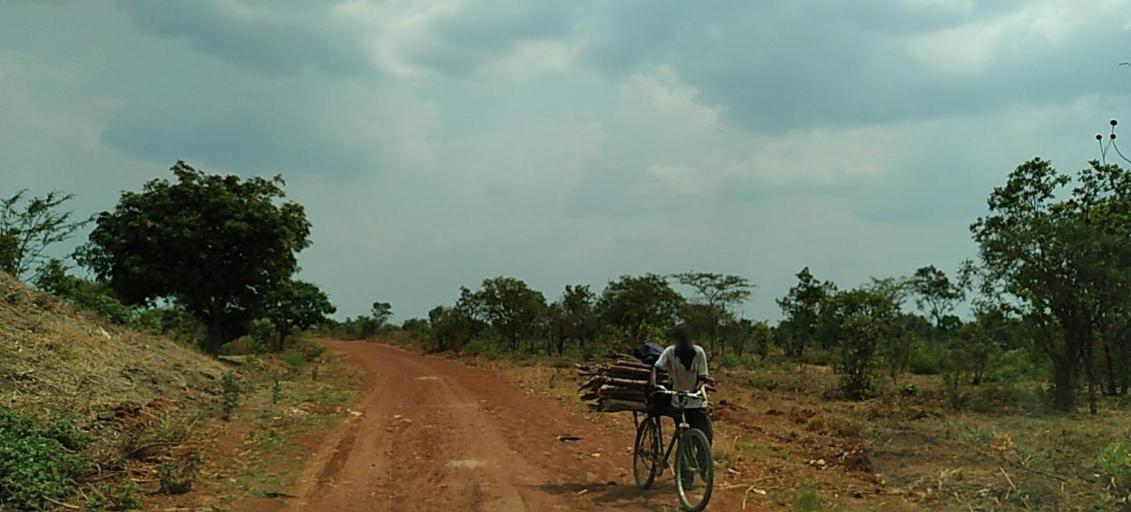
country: ZM
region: Copperbelt
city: Kalulushi
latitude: -12.8775
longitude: 28.0747
